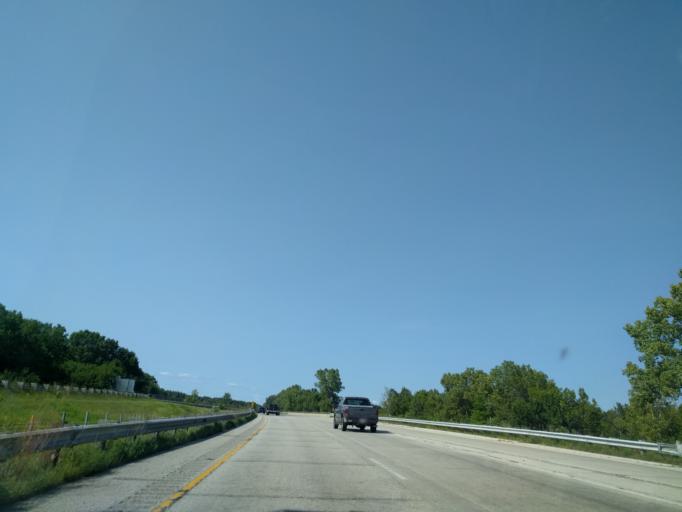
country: US
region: Wisconsin
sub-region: Brown County
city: Suamico
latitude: 44.6393
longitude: -88.0461
